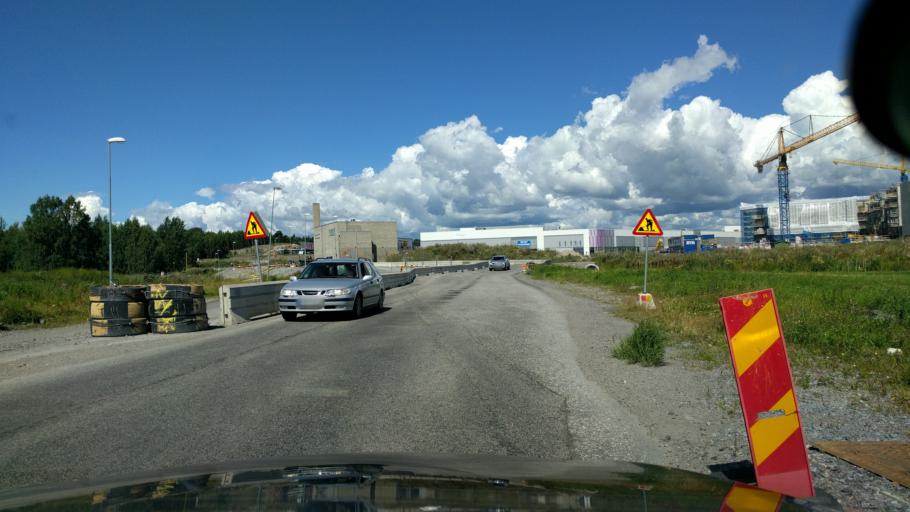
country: SE
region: Stockholm
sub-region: Jarfalla Kommun
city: Jakobsberg
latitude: 59.4085
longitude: 17.8656
